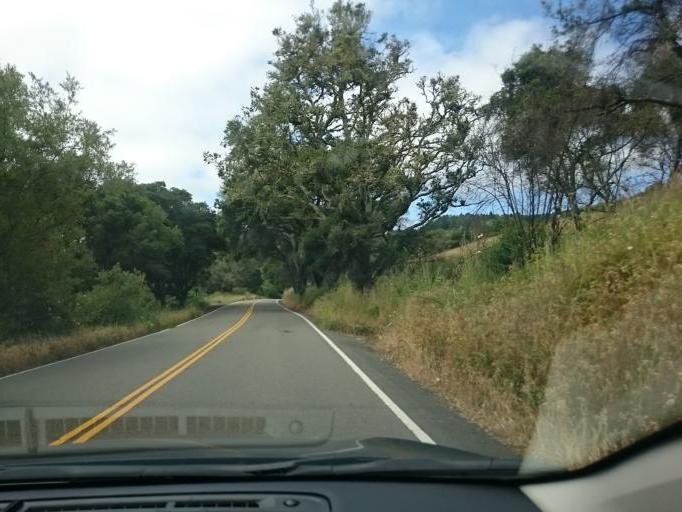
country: US
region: California
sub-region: Marin County
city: Bolinas
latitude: 37.9507
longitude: -122.7125
